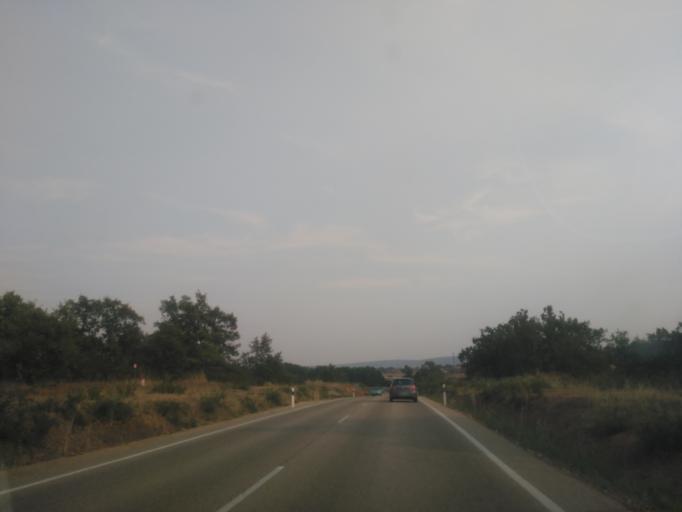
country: ES
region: Castille and Leon
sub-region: Provincia de Zamora
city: Tabara
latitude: 41.8396
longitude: -5.9750
